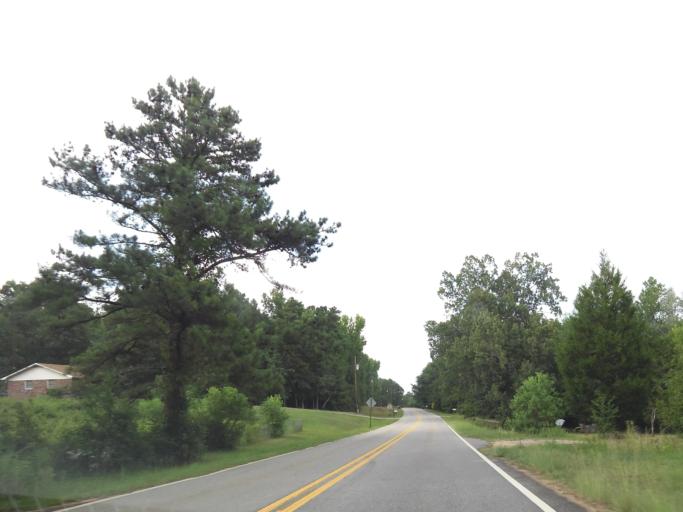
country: US
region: Georgia
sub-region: Bibb County
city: West Point
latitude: 32.8154
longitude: -83.8457
